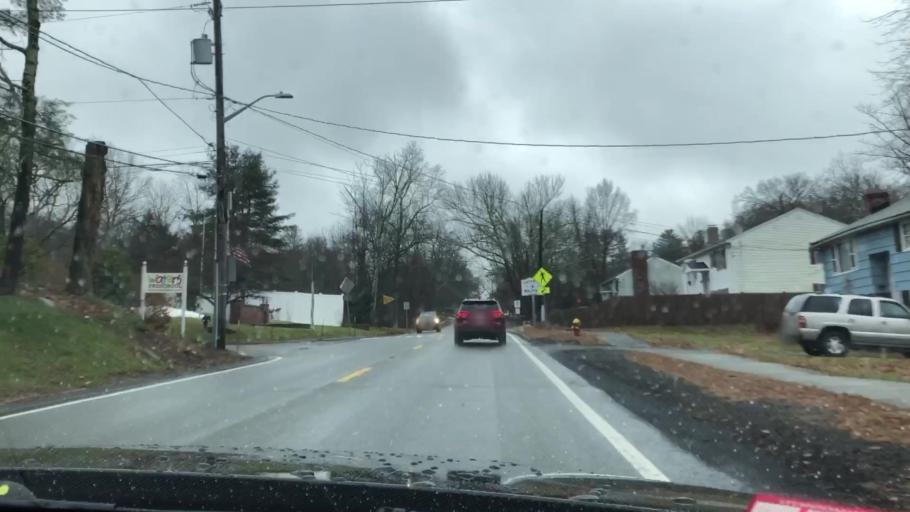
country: US
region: Massachusetts
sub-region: Norfolk County
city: Norwood
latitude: 42.1722
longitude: -71.2258
